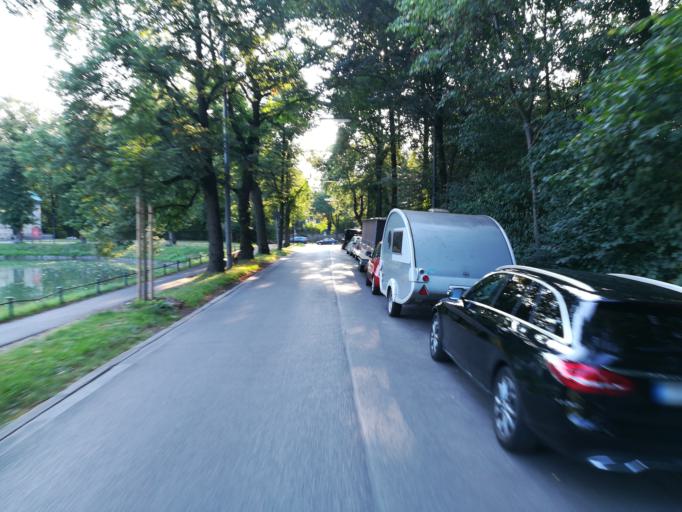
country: DE
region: Bavaria
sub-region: Upper Bavaria
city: Munich
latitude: 48.1587
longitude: 11.5286
